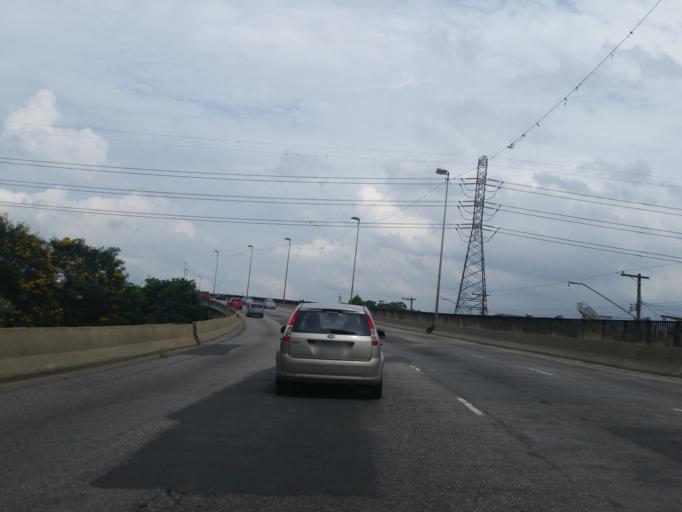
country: BR
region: Sao Paulo
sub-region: Guarulhos
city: Guarulhos
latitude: -23.5128
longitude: -46.4571
